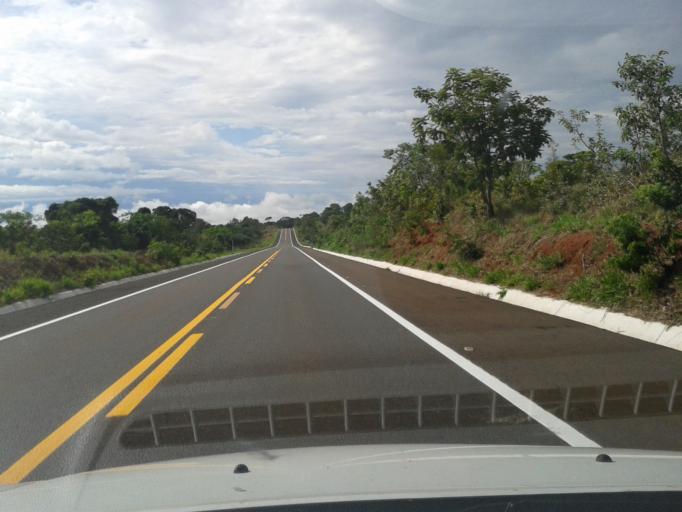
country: BR
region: Minas Gerais
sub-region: Campina Verde
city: Campina Verde
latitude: -19.3159
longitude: -49.6616
